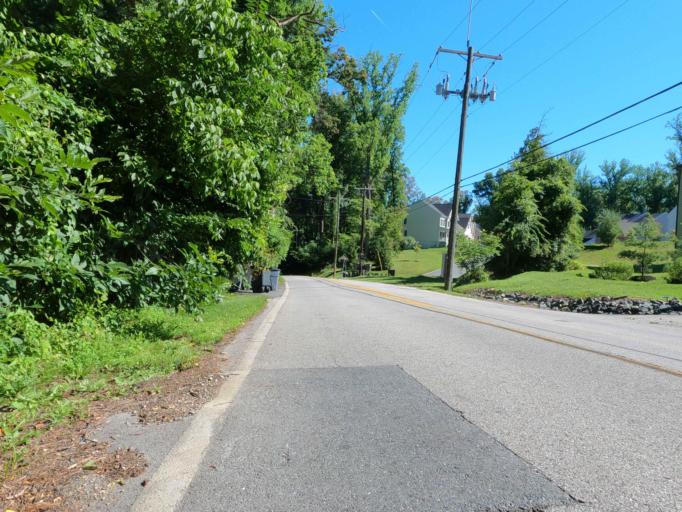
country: US
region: Maryland
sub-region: Howard County
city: Highland
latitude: 39.1984
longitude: -76.9220
